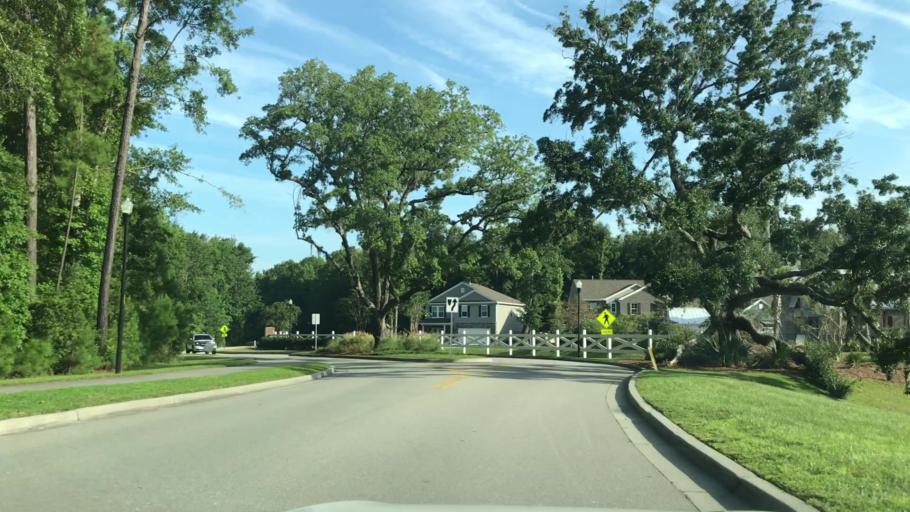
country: US
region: South Carolina
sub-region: Charleston County
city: Isle of Palms
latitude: 32.8889
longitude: -79.7482
